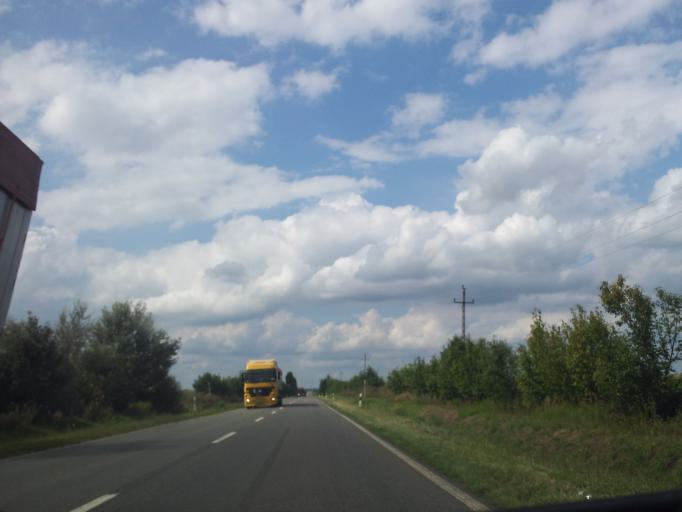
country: HU
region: Baranya
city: Mohacs
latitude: 45.9791
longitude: 18.6623
